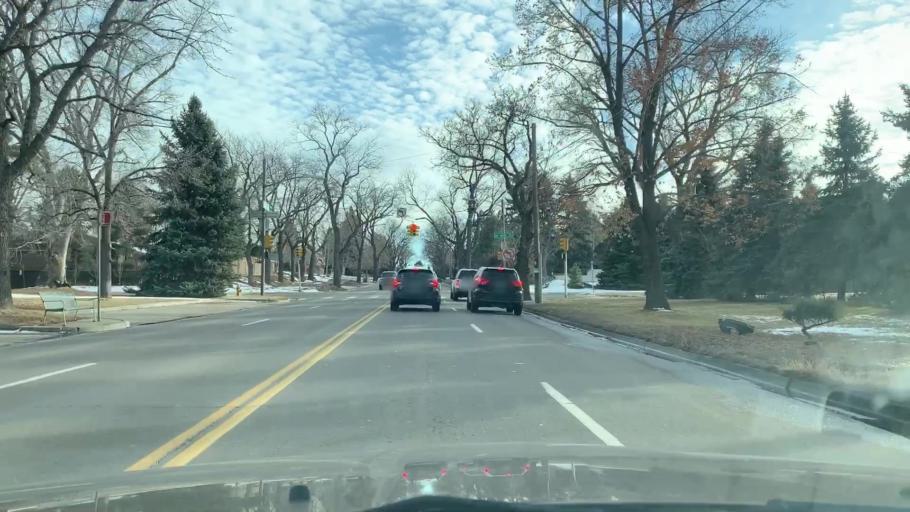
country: US
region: Colorado
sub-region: Arapahoe County
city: Glendale
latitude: 39.7225
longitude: -104.9128
